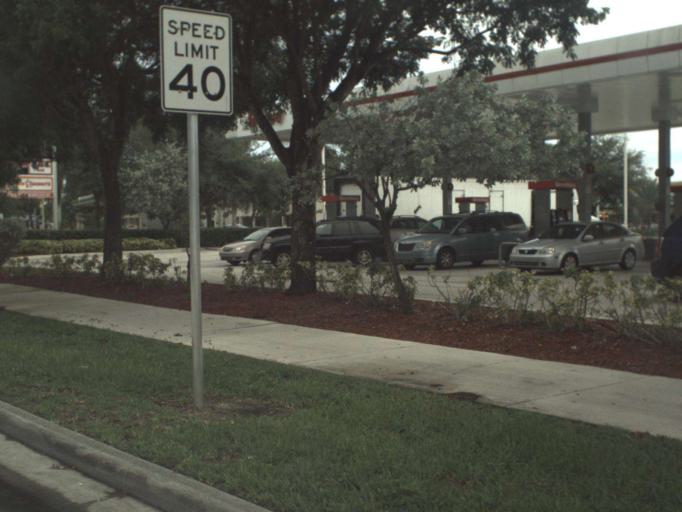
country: US
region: Florida
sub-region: Miami-Dade County
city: Country Club
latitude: 25.9423
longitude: -80.3230
